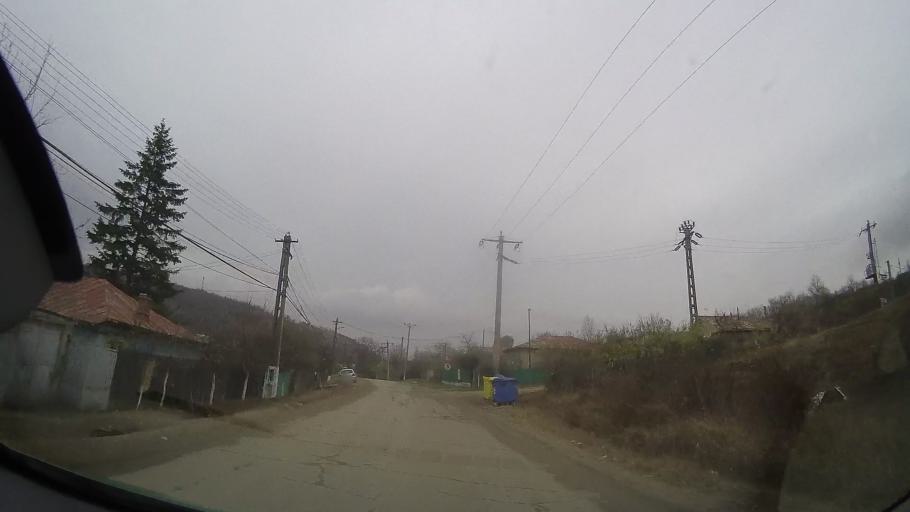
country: RO
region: Prahova
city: Ceptura de Sus
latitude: 45.0452
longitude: 26.3059
